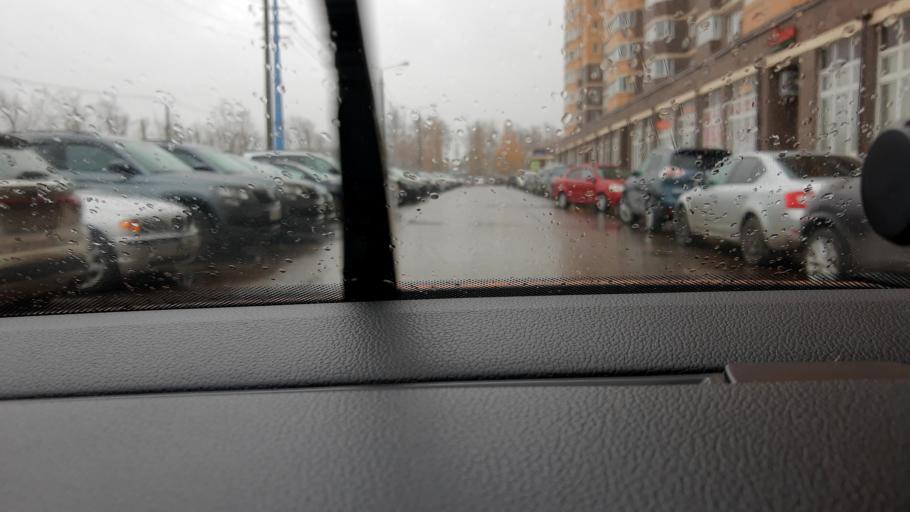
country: RU
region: Moskovskaya
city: Dolgoprudnyy
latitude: 55.9629
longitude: 37.5304
